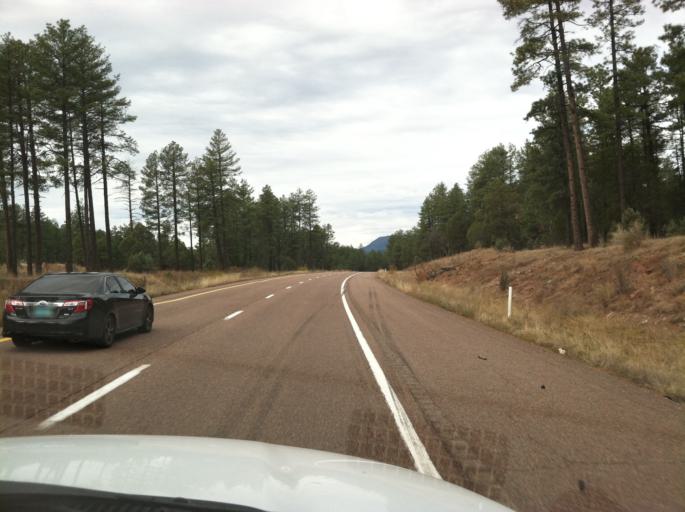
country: US
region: Arizona
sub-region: Gila County
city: Star Valley
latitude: 34.2947
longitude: -110.9785
